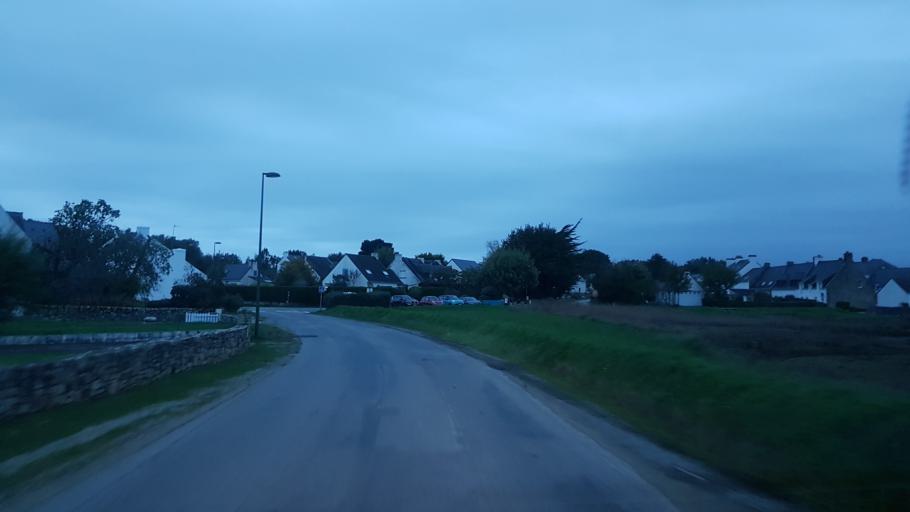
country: FR
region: Brittany
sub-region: Departement du Morbihan
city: Sarzeau
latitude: 47.5406
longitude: -2.8066
